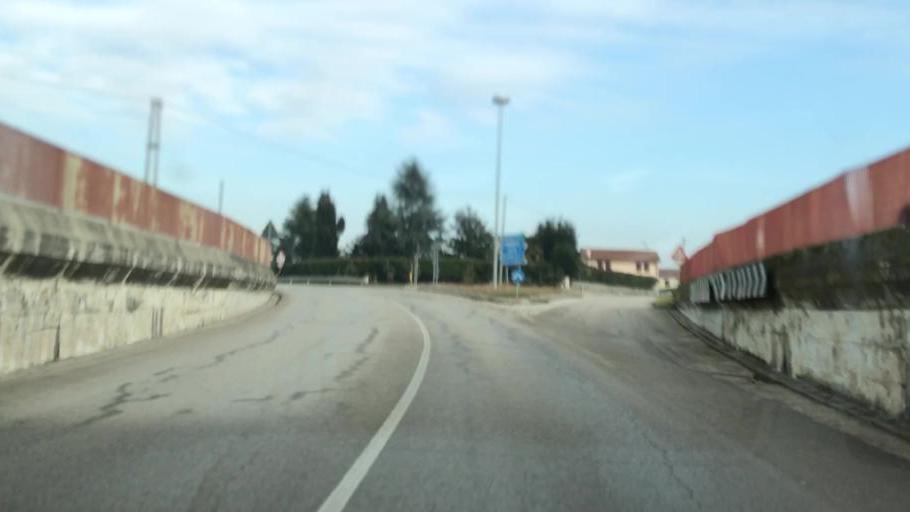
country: IT
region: Veneto
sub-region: Provincia di Rovigo
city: Fratta Polesine
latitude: 45.0377
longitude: 11.6516
